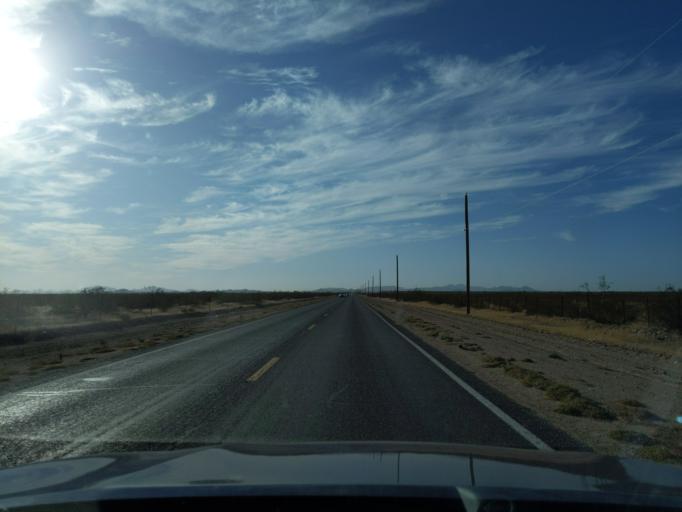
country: US
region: Arizona
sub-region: Pinal County
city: Florence
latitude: 33.1183
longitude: -111.3774
